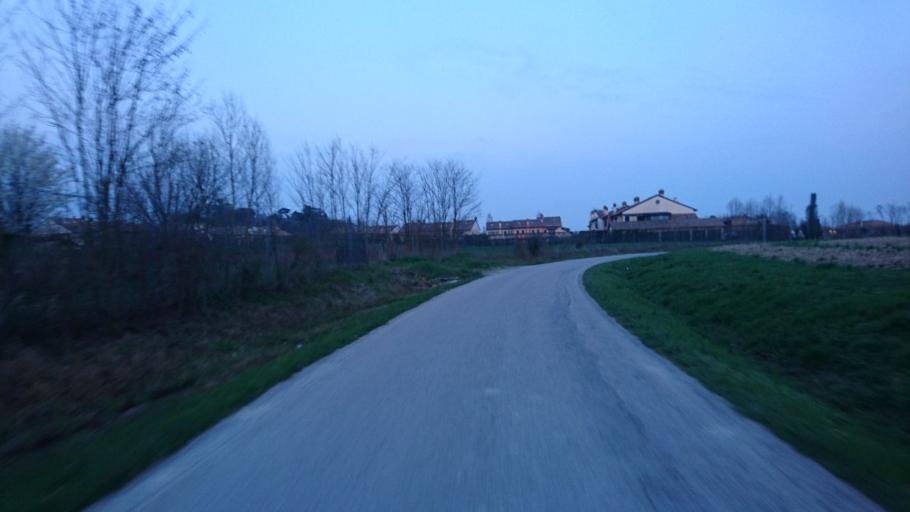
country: IT
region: Veneto
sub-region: Provincia di Padova
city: Saccolongo
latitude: 45.3847
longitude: 11.7587
